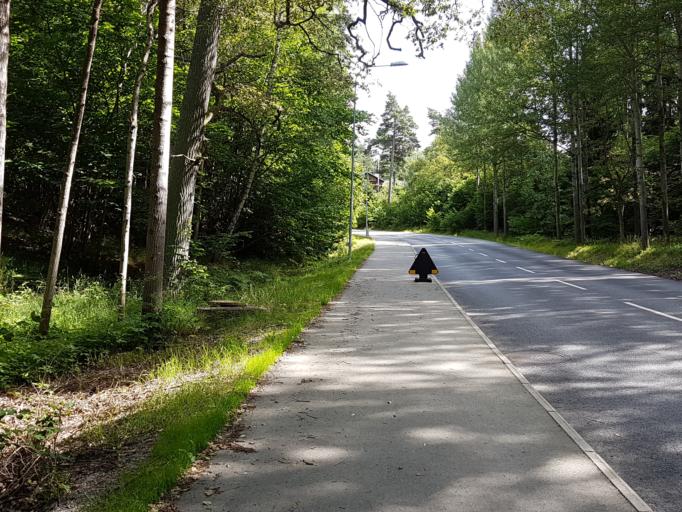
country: SE
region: Stockholm
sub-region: Nacka Kommun
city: Kummelnas
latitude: 59.3462
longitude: 18.2448
